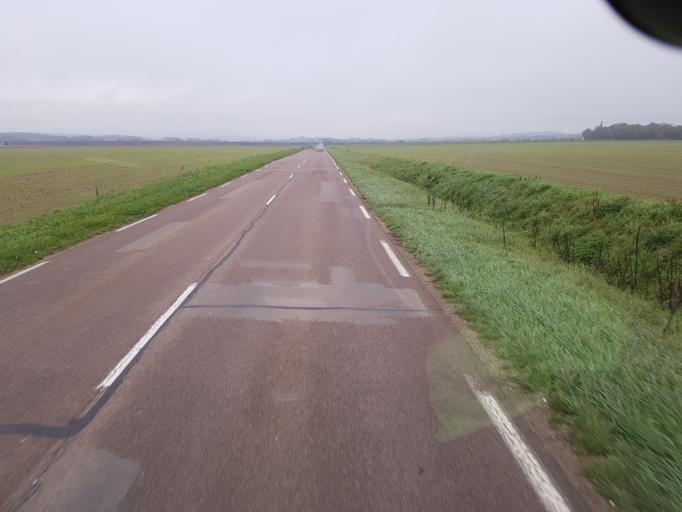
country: FR
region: Bourgogne
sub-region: Departement de la Cote-d'Or
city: Marcilly-sur-Tille
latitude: 47.4969
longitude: 5.2039
